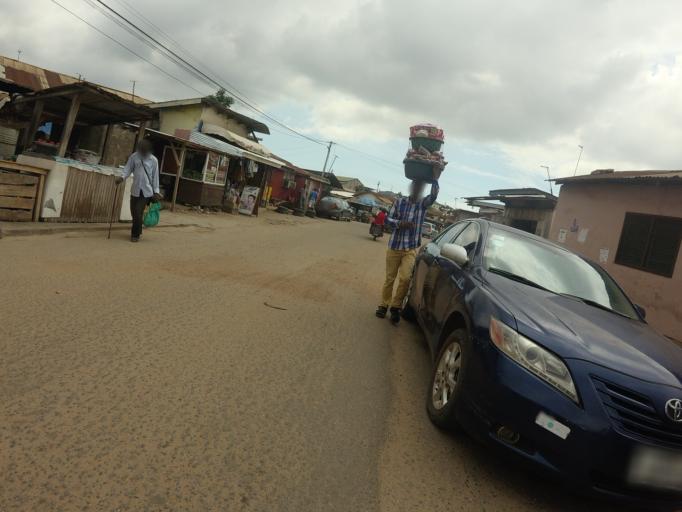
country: GH
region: Greater Accra
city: Accra
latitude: 5.5881
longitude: -0.2002
